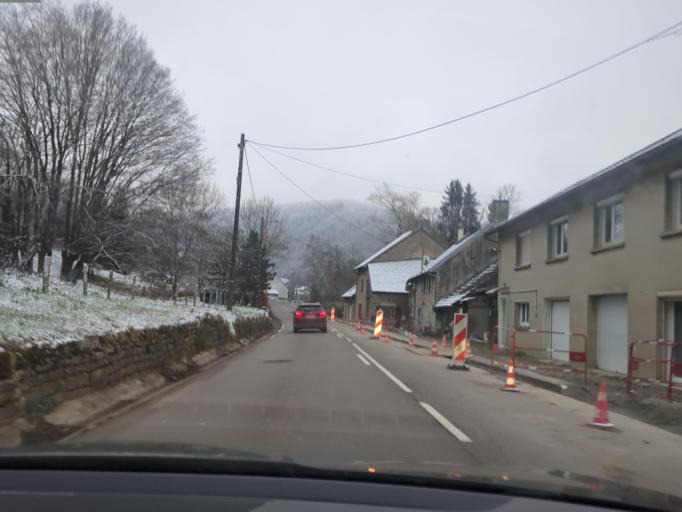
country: FR
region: Franche-Comte
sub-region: Departement du Jura
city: Perrigny
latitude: 46.6428
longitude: 5.6019
